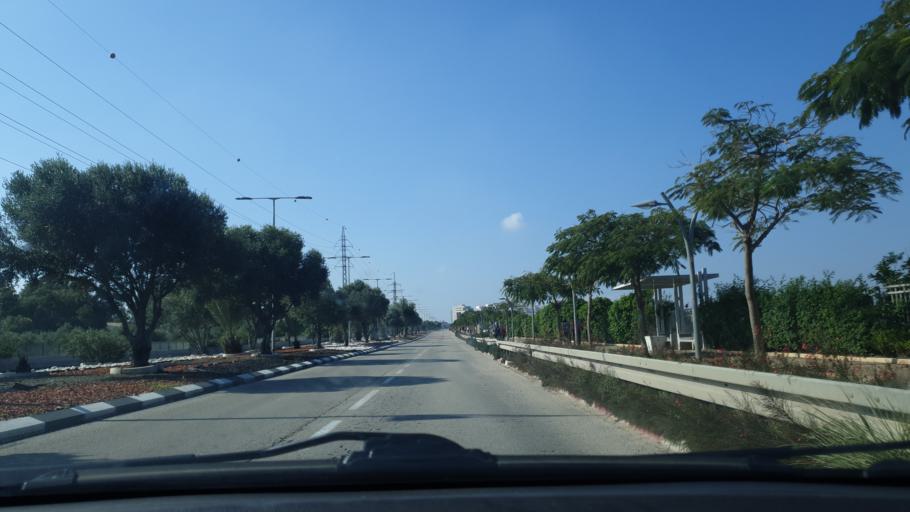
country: IL
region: Central District
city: Kefar Habad
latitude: 31.9721
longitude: 34.8355
